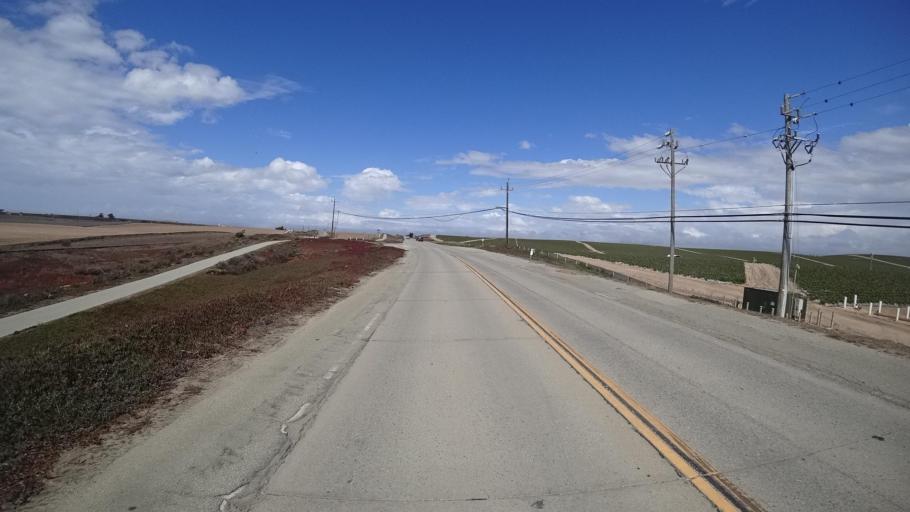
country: US
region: California
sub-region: Monterey County
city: Marina
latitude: 36.7046
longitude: -121.7889
